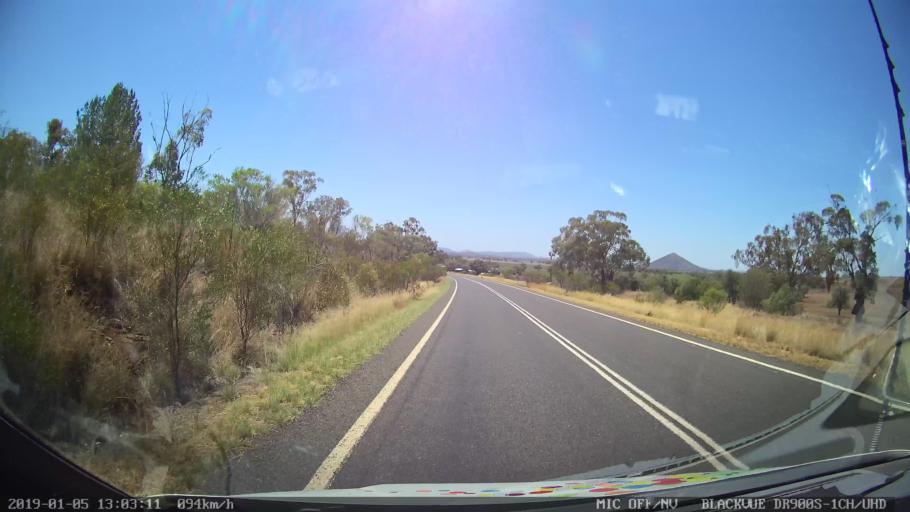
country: AU
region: New South Wales
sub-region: Gunnedah
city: Gunnedah
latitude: -31.1122
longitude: 149.8235
